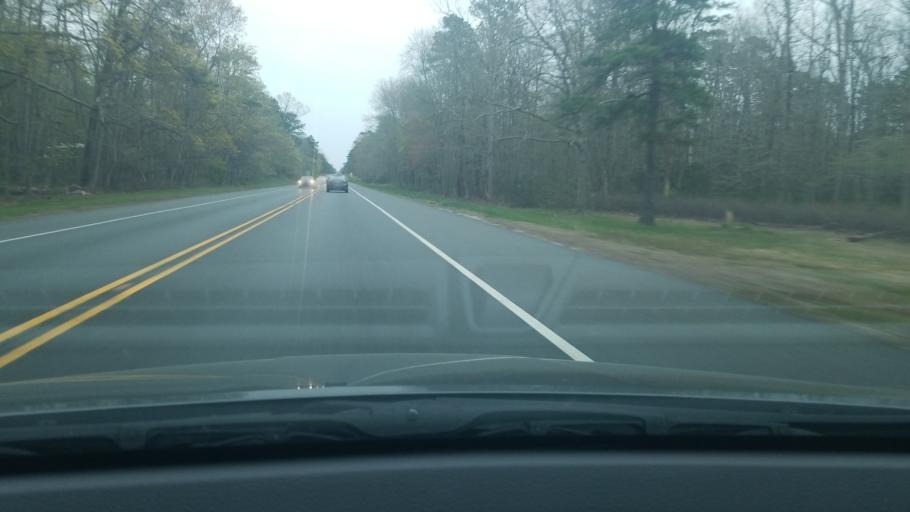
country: US
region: New Jersey
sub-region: Burlington County
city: Leisuretowne
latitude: 39.8862
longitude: -74.6813
